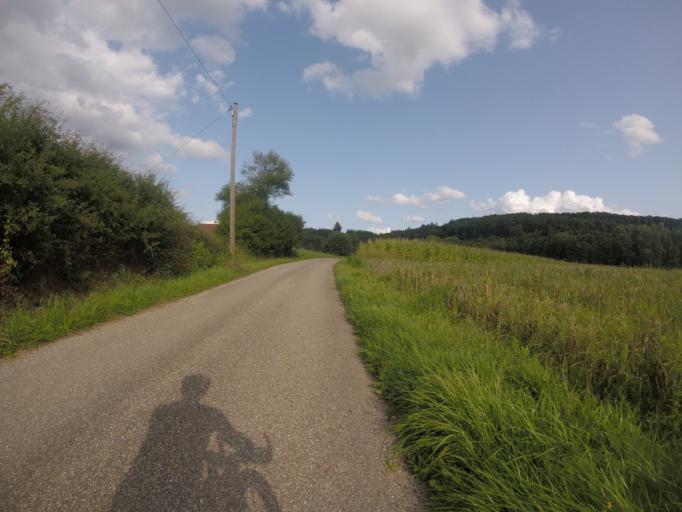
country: DE
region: Baden-Wuerttemberg
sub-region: Regierungsbezirk Stuttgart
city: Aspach
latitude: 48.9908
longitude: 9.4129
